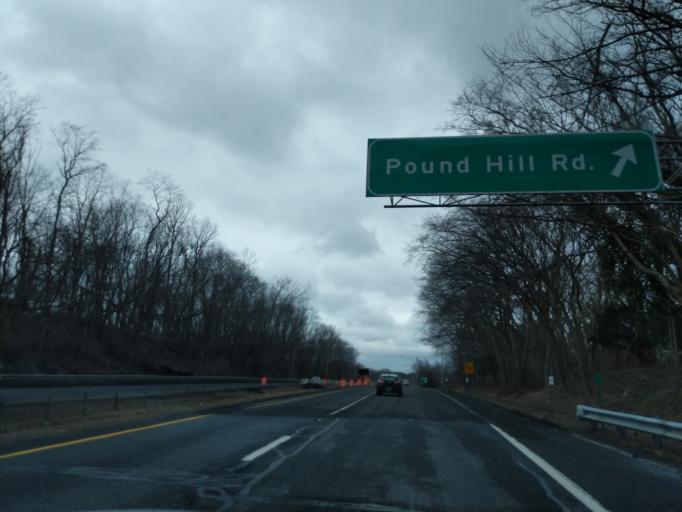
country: US
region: Rhode Island
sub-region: Providence County
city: North Smithfield
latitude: 41.9859
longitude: -71.5481
